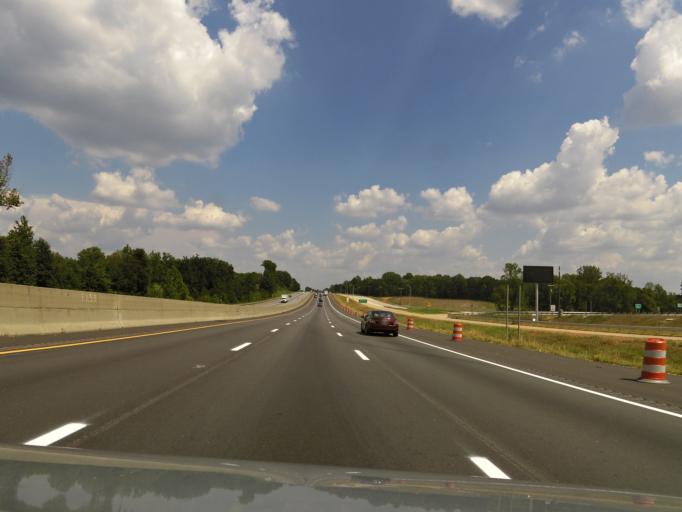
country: US
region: North Carolina
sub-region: Gaston County
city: Bessemer City
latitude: 35.2611
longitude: -81.2806
